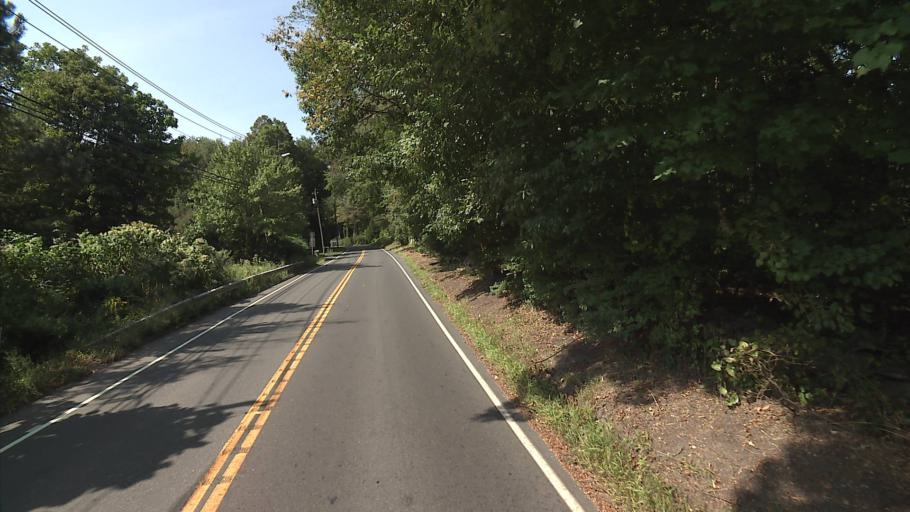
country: US
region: Connecticut
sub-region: Fairfield County
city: Fairfield
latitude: 41.2039
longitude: -73.2728
